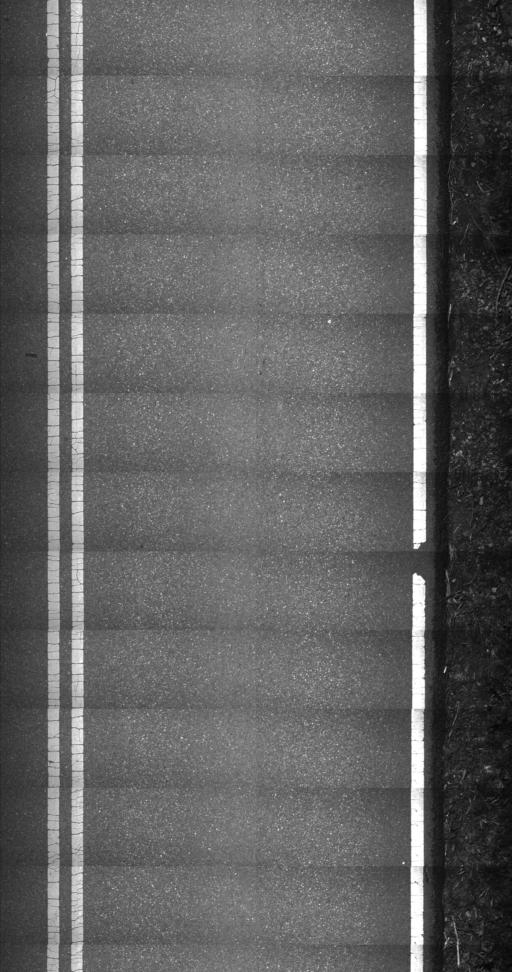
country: US
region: Vermont
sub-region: Lamoille County
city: Johnson
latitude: 44.5472
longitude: -72.7929
